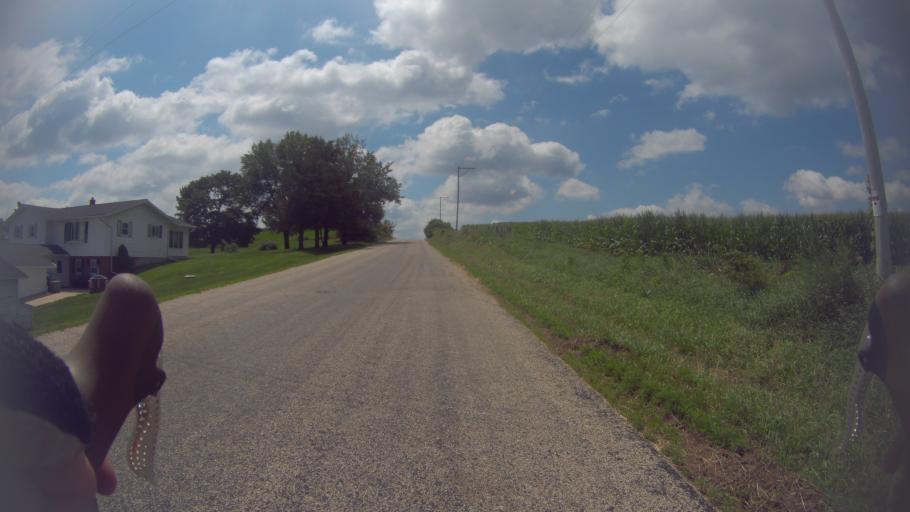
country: US
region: Wisconsin
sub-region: Sauk County
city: Sauk City
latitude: 43.2341
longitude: -89.6405
